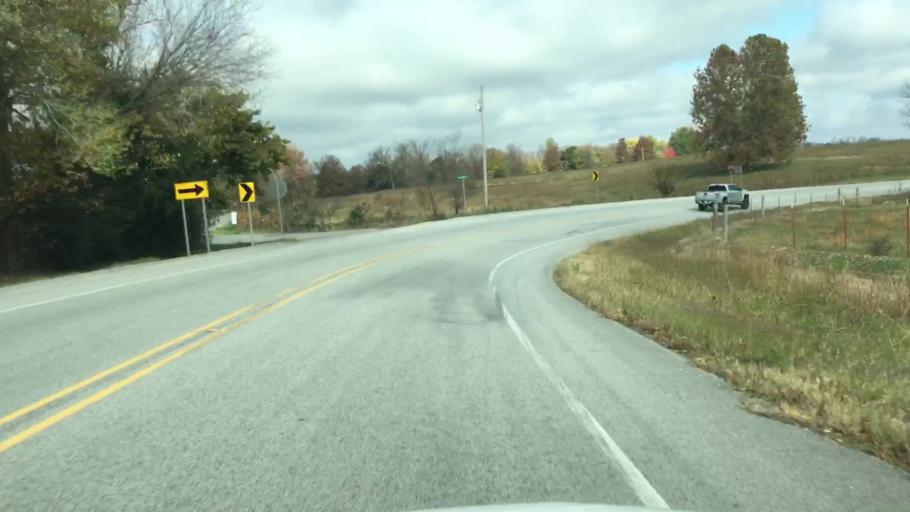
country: US
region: Arkansas
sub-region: Benton County
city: Centerton
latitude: 36.2987
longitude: -94.3408
